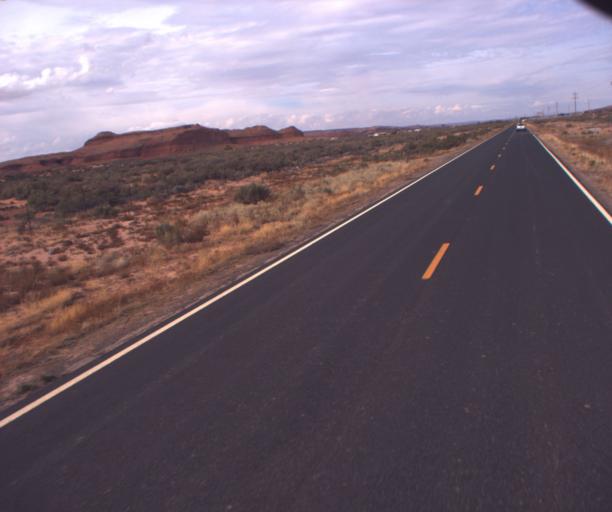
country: US
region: Arizona
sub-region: Apache County
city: Many Farms
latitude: 36.7032
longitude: -109.6182
